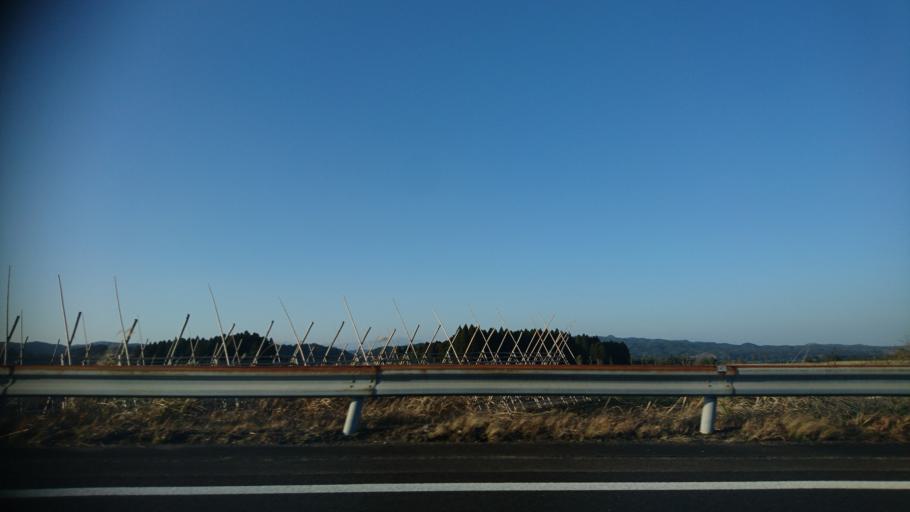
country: JP
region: Miyazaki
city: Miyazaki-shi
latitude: 31.8204
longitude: 131.2814
